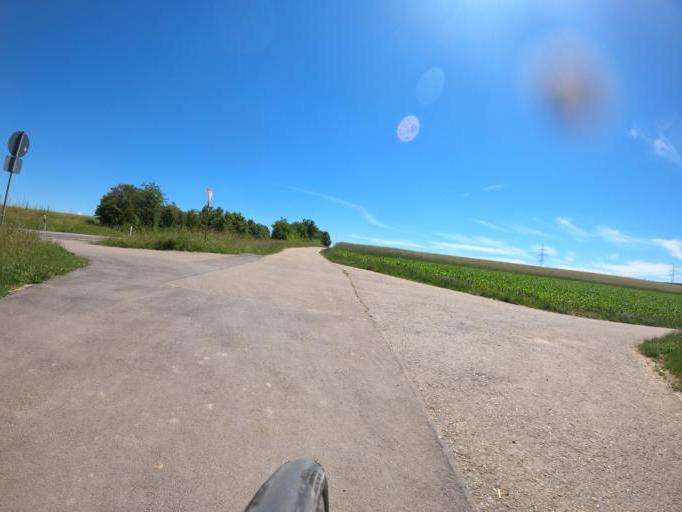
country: DE
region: Baden-Wuerttemberg
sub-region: Regierungsbezirk Stuttgart
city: Eberdingen
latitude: 48.9060
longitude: 8.9395
